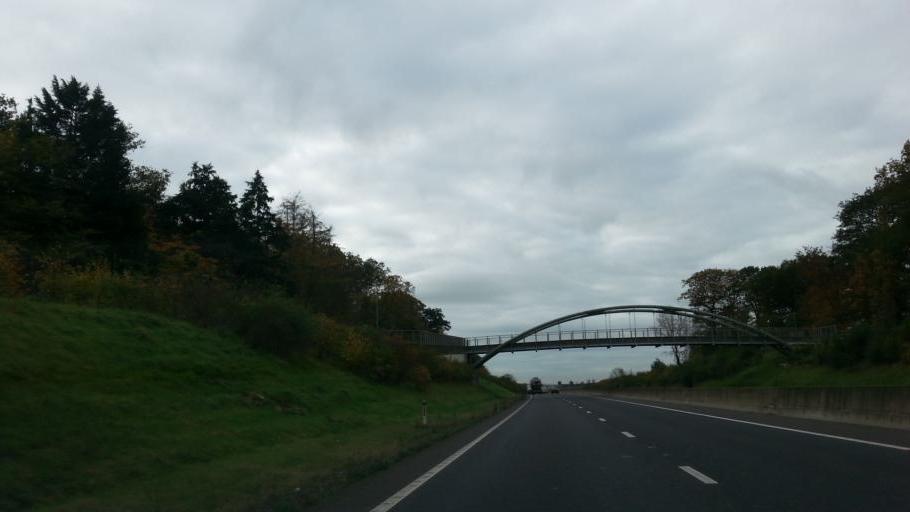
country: GB
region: England
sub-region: Nottinghamshire
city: Farndon
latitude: 53.0134
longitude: -0.9059
